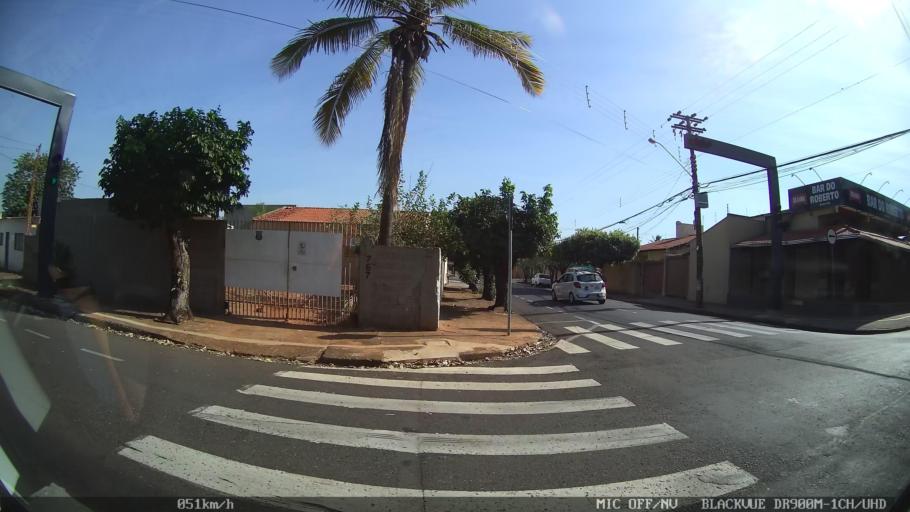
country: BR
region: Sao Paulo
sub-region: Sao Jose Do Rio Preto
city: Sao Jose do Rio Preto
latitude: -20.8001
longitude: -49.4169
